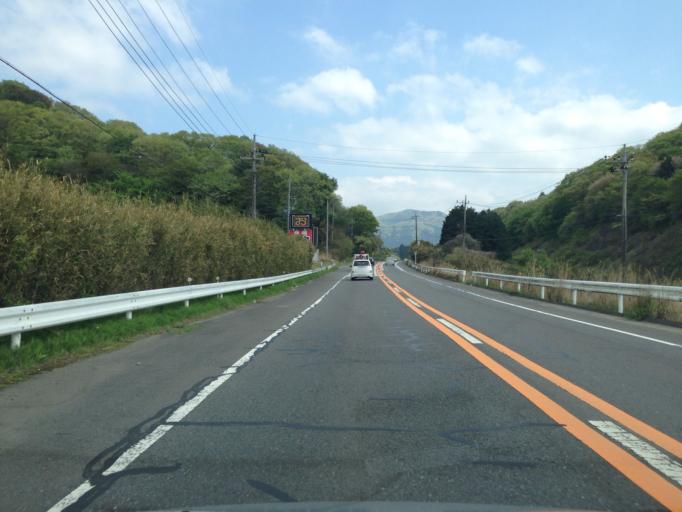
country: JP
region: Ibaraki
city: Iwase
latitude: 36.3528
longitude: 140.1635
